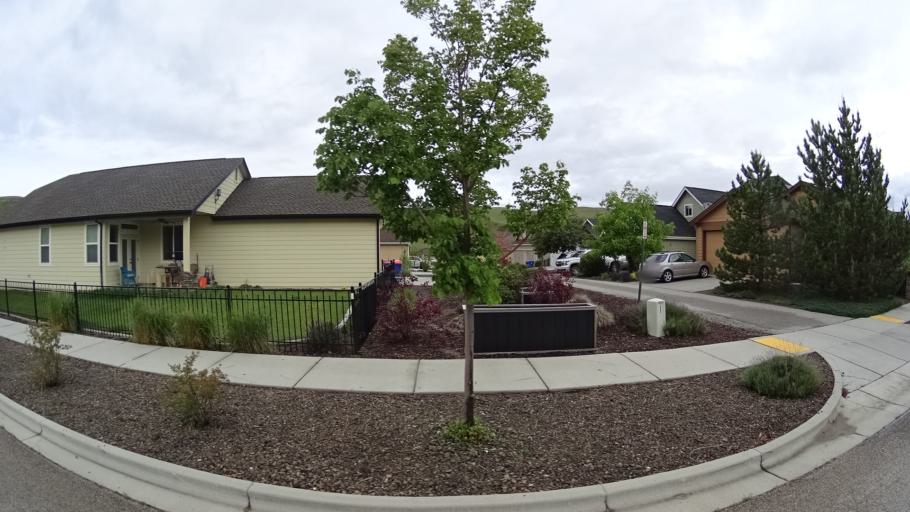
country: US
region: Idaho
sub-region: Ada County
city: Eagle
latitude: 43.7712
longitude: -116.2621
